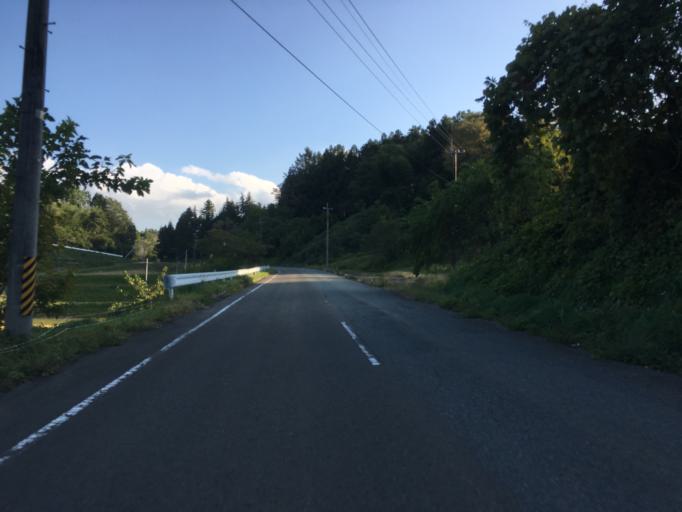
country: JP
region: Fukushima
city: Nihommatsu
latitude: 37.6413
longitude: 140.5529
